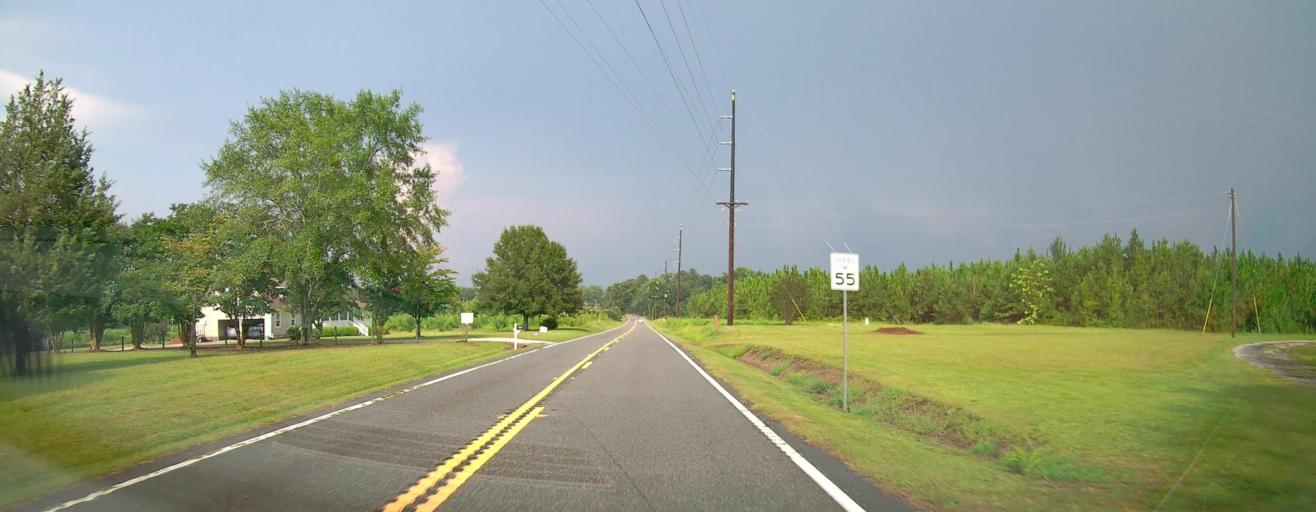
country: US
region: Georgia
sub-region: Twiggs County
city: Jeffersonville
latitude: 32.6042
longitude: -83.2917
